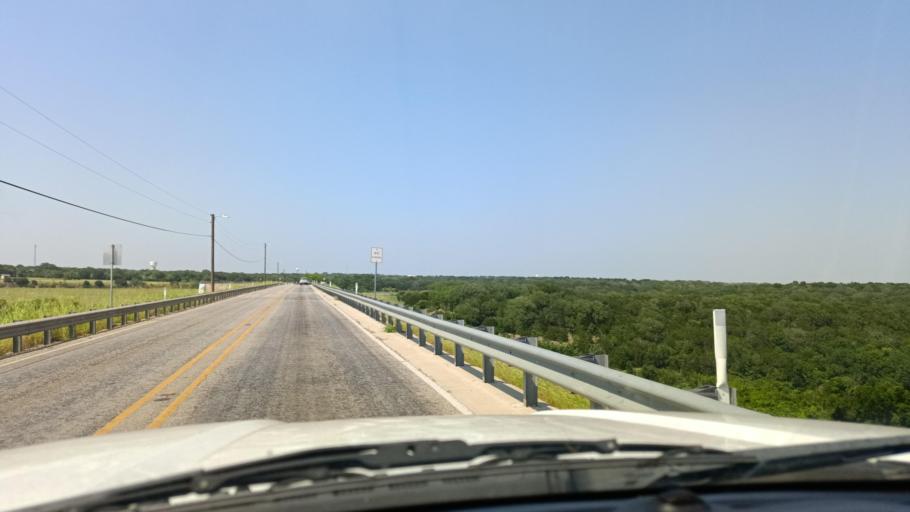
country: US
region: Texas
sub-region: Bell County
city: Morgans Point Resort
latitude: 31.1089
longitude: -97.4725
